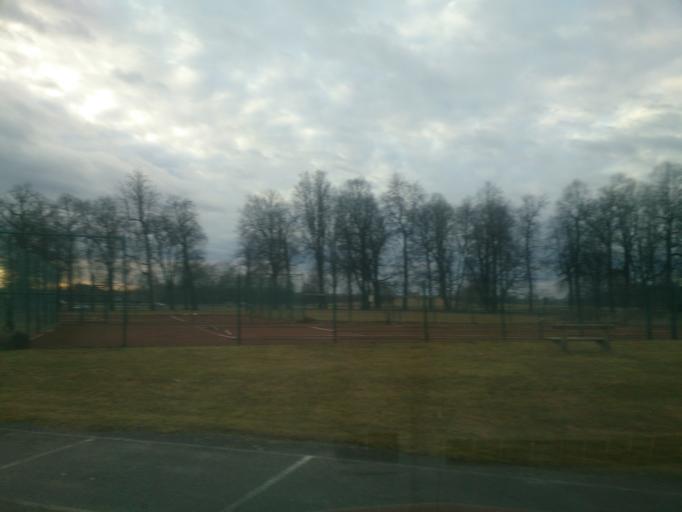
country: SE
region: OEstergoetland
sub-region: Norrkopings Kommun
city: Norrkoping
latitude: 58.5894
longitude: 16.1562
